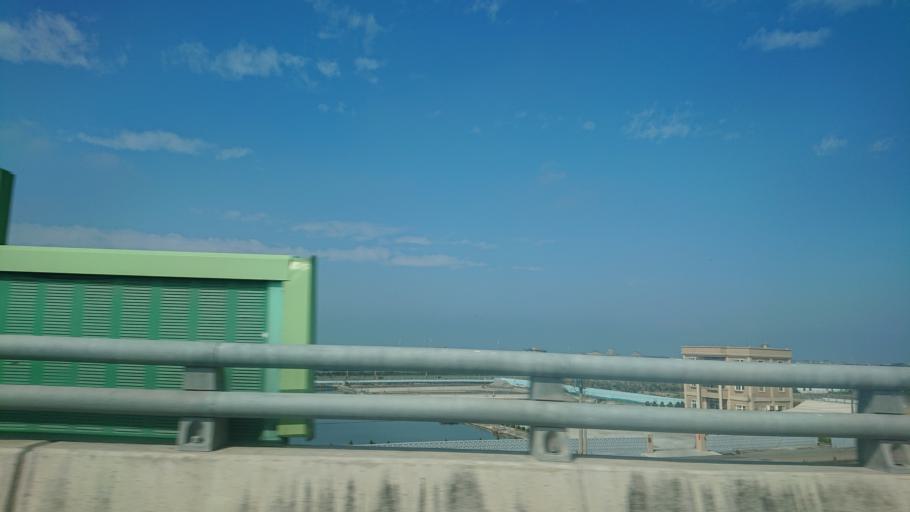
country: TW
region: Taiwan
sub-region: Changhua
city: Chang-hua
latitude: 24.0428
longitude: 120.4059
